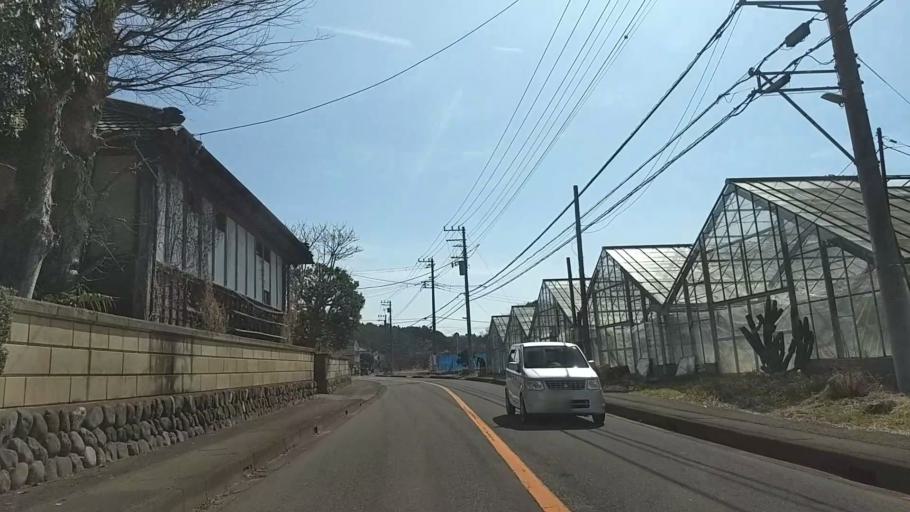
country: JP
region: Kanagawa
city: Fujisawa
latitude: 35.3793
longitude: 139.4287
